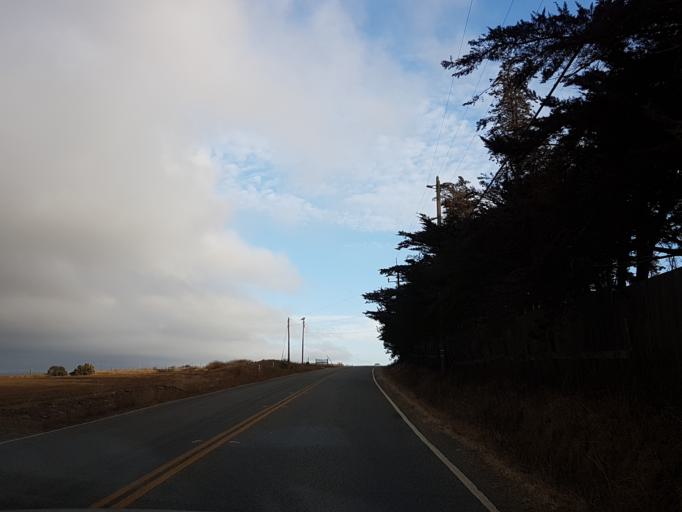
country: US
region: California
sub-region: Monterey County
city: Chualar
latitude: 36.5924
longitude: -121.6107
